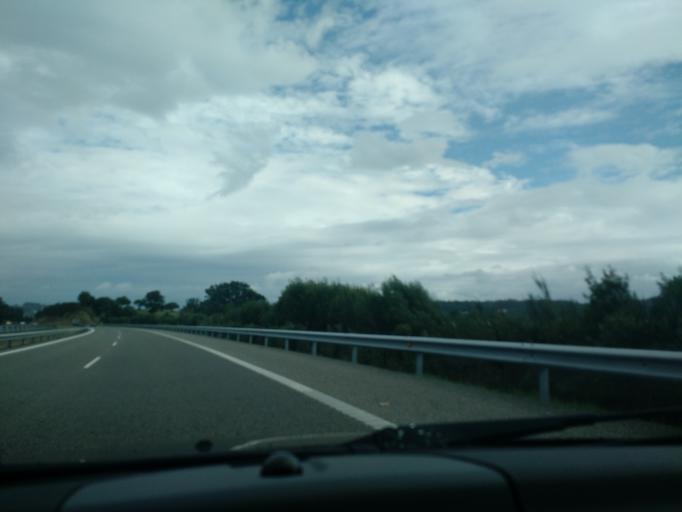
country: ES
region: Galicia
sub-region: Provincia da Coruna
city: Abegondo
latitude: 43.2402
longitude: -8.2569
